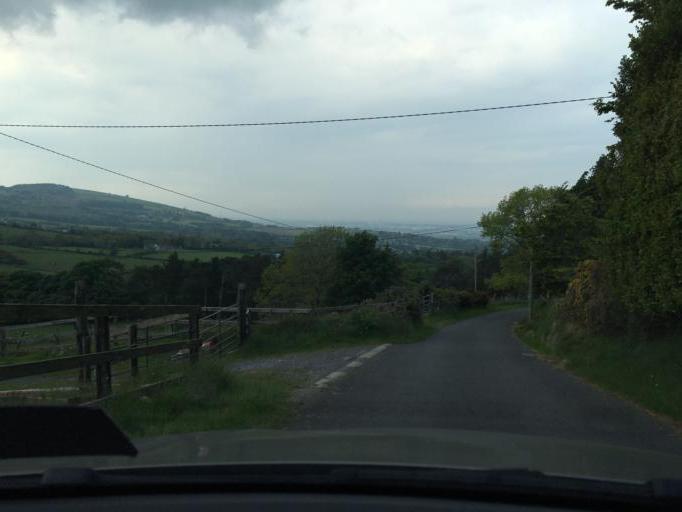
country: IE
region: Leinster
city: Ballinteer
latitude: 53.2497
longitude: -6.2772
